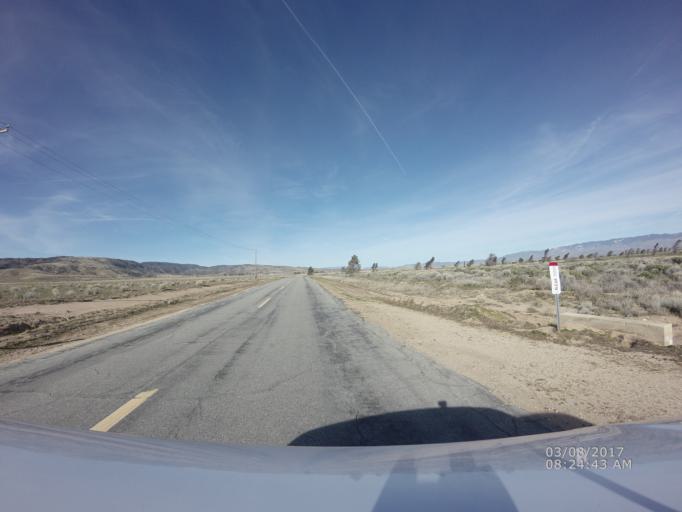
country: US
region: California
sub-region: Los Angeles County
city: Green Valley
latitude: 34.7389
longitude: -118.4605
